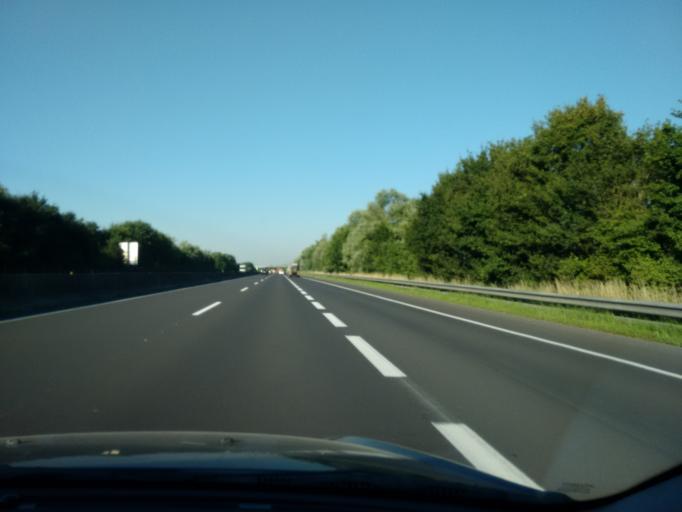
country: AT
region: Upper Austria
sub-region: Wels Stadt
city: Wels
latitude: 48.1695
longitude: 13.9888
